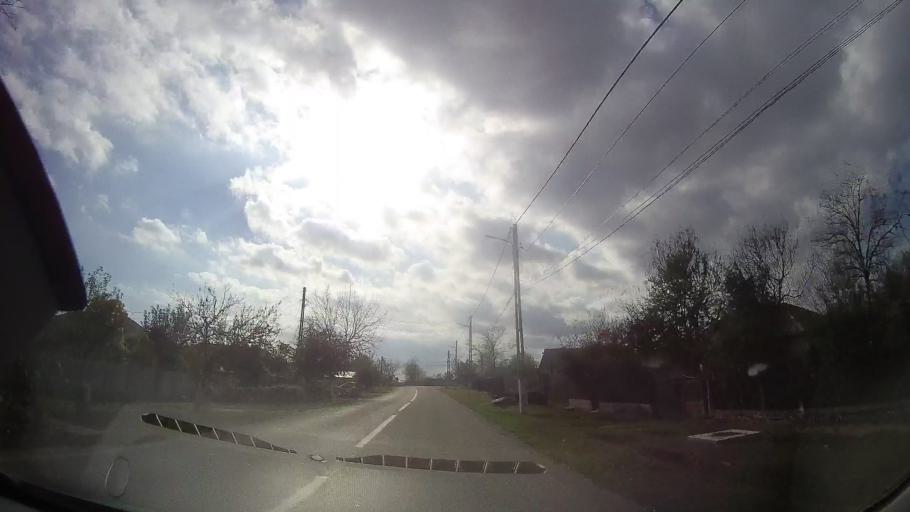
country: RO
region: Constanta
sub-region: Comuna Pecineaga
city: Pecineaga
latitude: 43.8960
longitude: 28.5109
